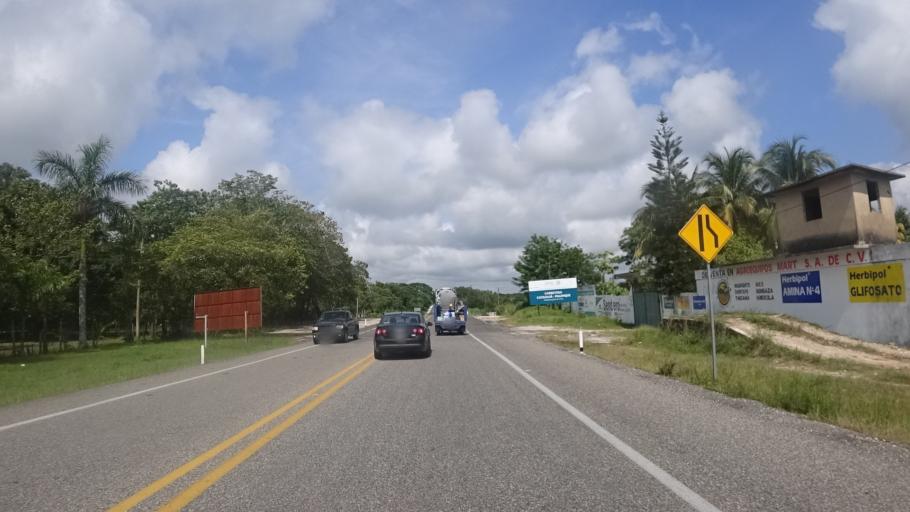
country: MX
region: Chiapas
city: Palenque
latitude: 17.5650
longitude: -92.0132
